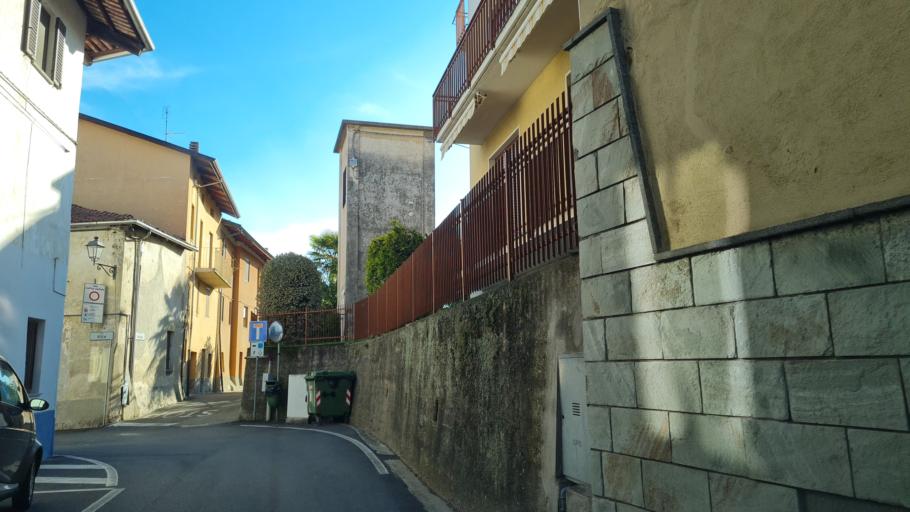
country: IT
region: Piedmont
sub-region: Provincia di Biella
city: Occhieppo Inferiore
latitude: 45.5523
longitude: 8.0231
